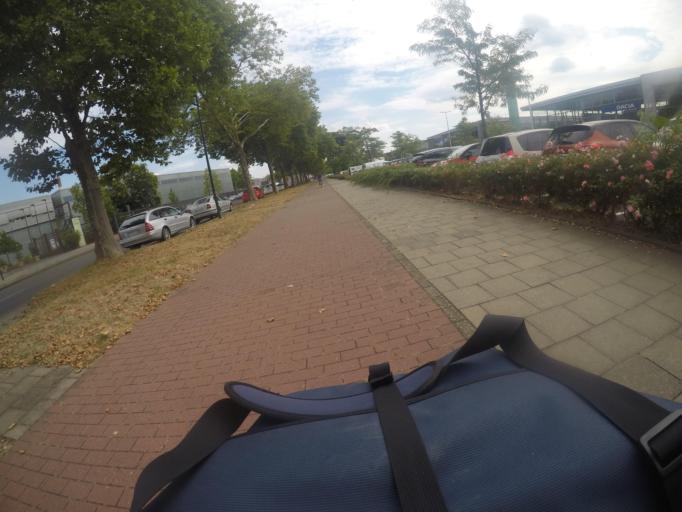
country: DE
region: North Rhine-Westphalia
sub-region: Regierungsbezirk Dusseldorf
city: Dusseldorf
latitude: 51.2217
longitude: 6.8177
